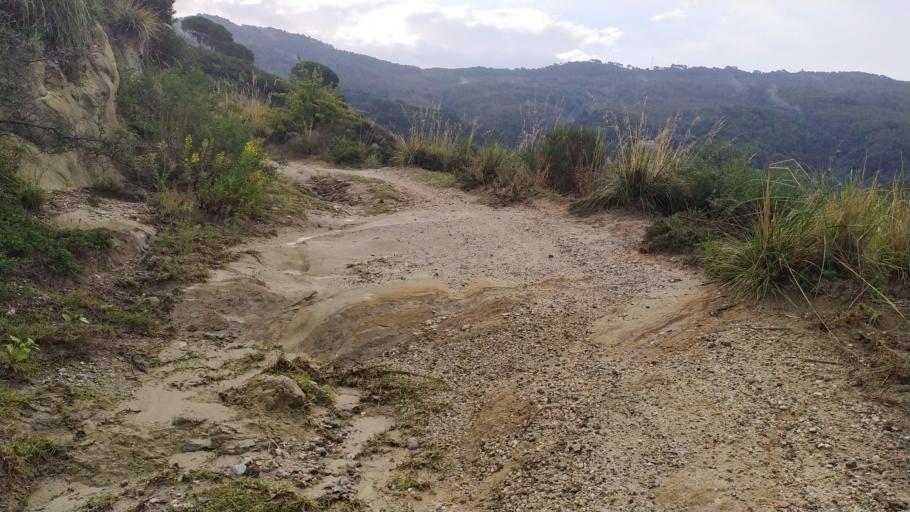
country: IT
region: Sicily
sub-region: Messina
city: Saponara
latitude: 38.2114
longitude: 15.4782
